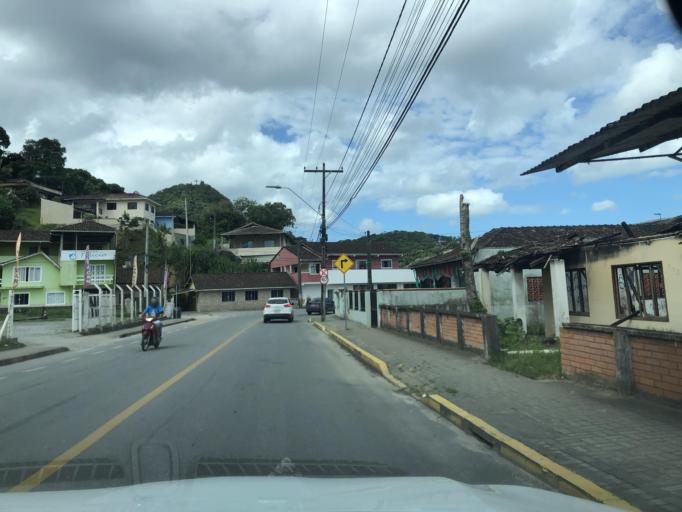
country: BR
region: Santa Catarina
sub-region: Sao Francisco Do Sul
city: Sao Francisco do Sul
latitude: -26.2431
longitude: -48.6299
